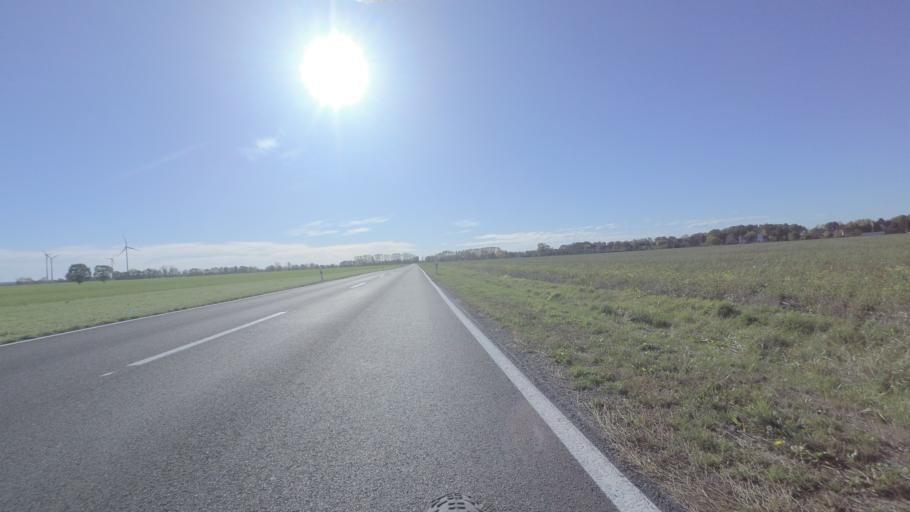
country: DE
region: Brandenburg
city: Elsterwerda
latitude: 51.4608
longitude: 13.4623
